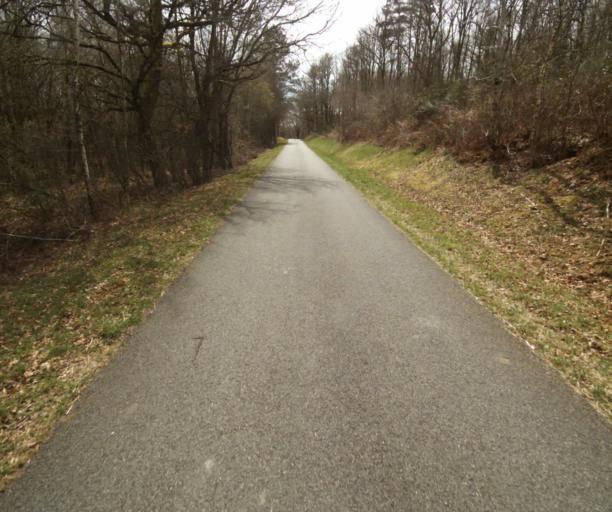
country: FR
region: Limousin
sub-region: Departement de la Correze
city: Egletons
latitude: 45.3724
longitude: 1.9668
